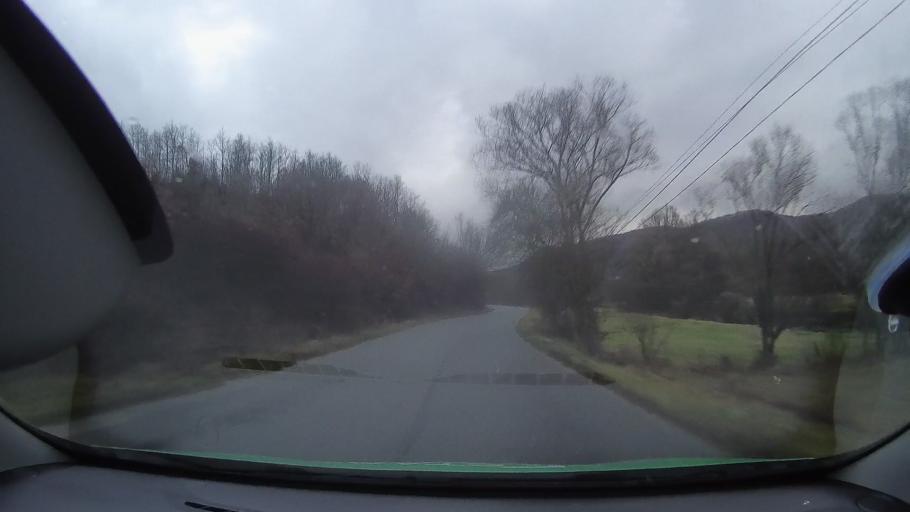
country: RO
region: Hunedoara
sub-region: Comuna Baia de Cris
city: Baia de Cris
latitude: 46.2043
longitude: 22.7169
